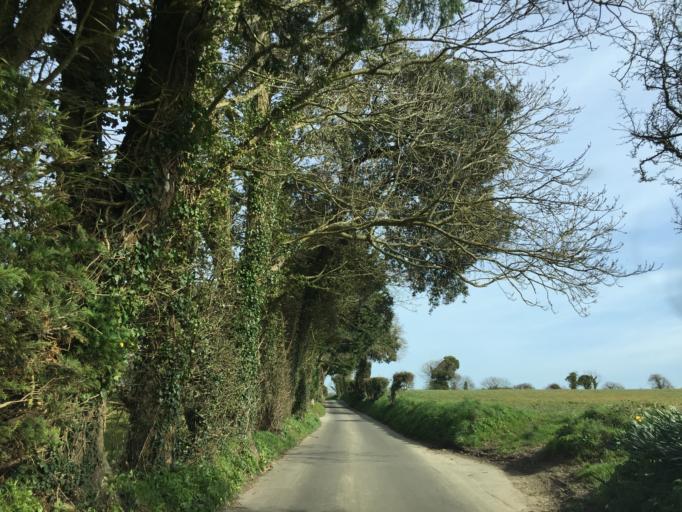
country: JE
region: St Helier
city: Saint Helier
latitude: 49.2200
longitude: -2.1397
